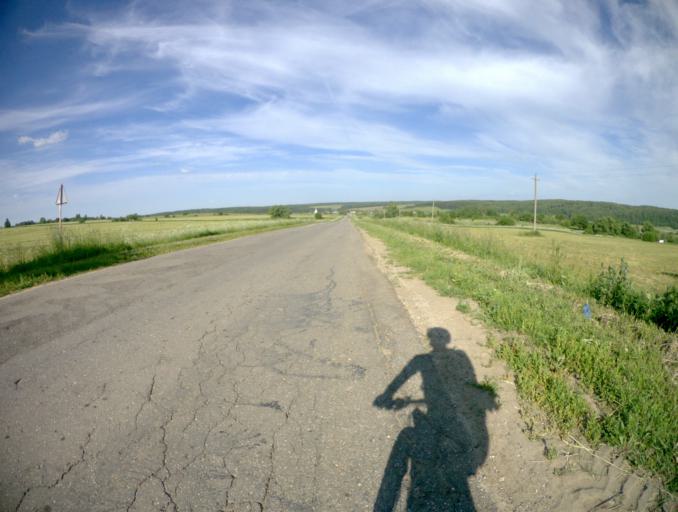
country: RU
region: Vladimir
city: Stavrovo
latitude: 56.1672
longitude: 40.1396
